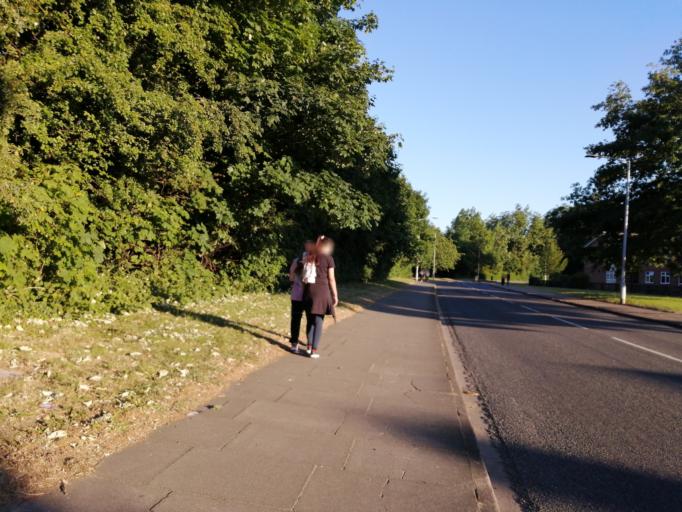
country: GB
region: England
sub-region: Peterborough
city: Peterborough
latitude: 52.5890
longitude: -0.2666
